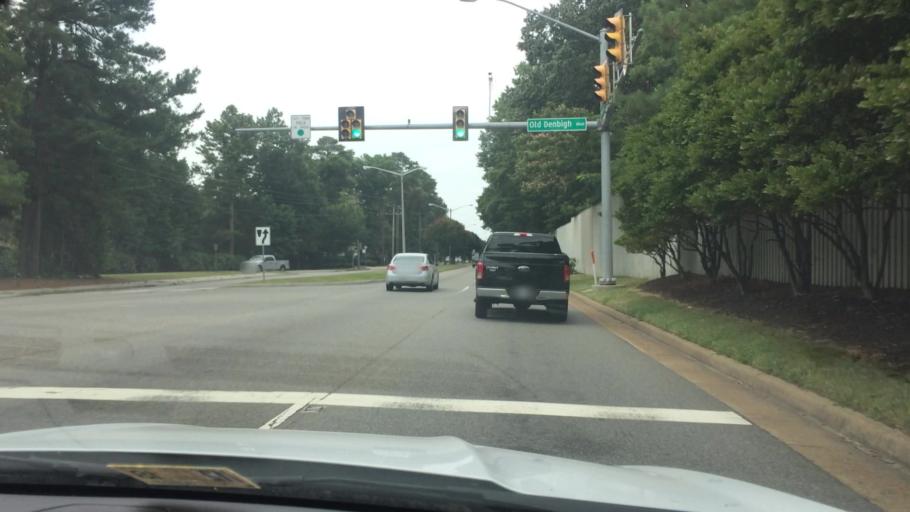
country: US
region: Virginia
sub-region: York County
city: Yorktown
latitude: 37.1495
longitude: -76.5102
